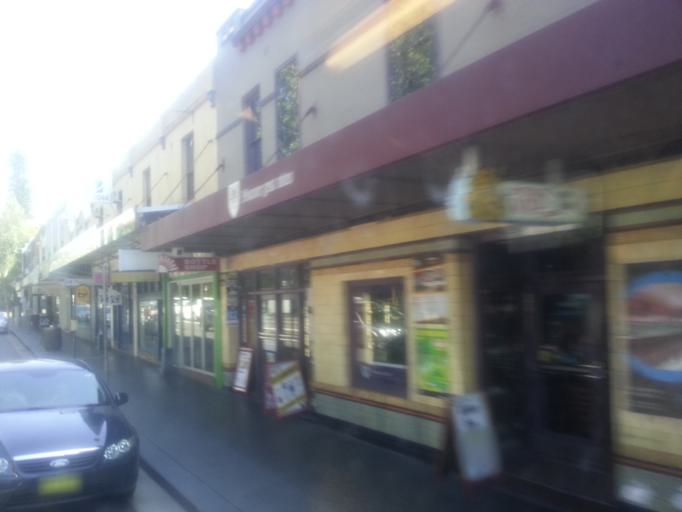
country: AU
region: New South Wales
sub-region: City of Sydney
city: Chippendale
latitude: -33.8796
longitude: 151.1869
